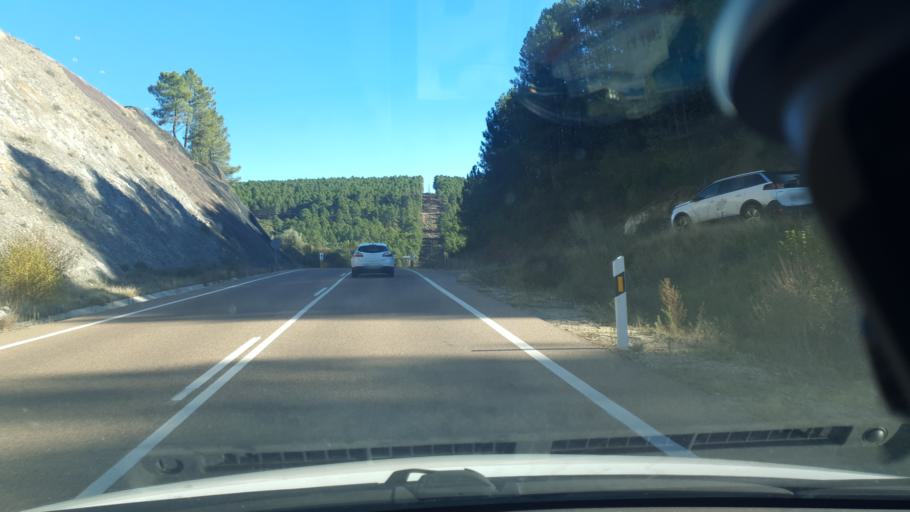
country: ES
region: Castille and Leon
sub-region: Provincia de Avila
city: Poyales del Hoyo
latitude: 40.1681
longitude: -5.1274
